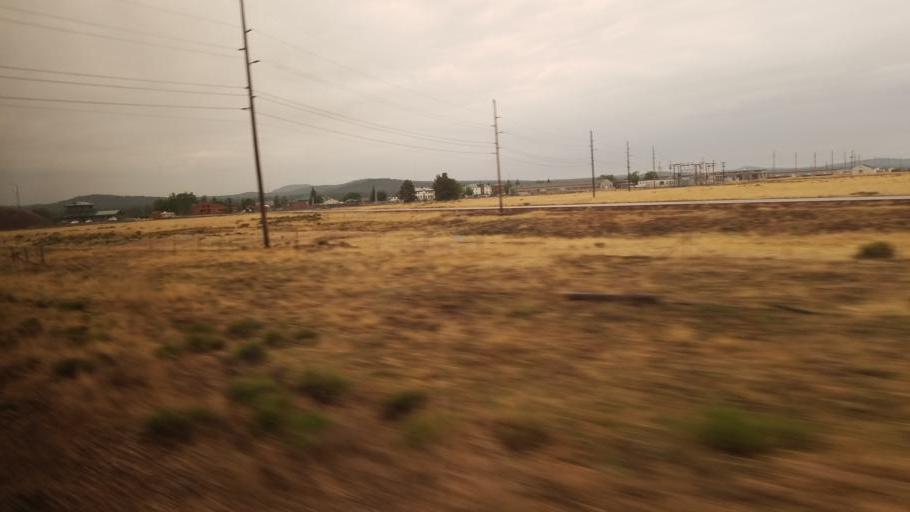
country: US
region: Arizona
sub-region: Coconino County
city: Parks
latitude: 35.2331
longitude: -111.8249
